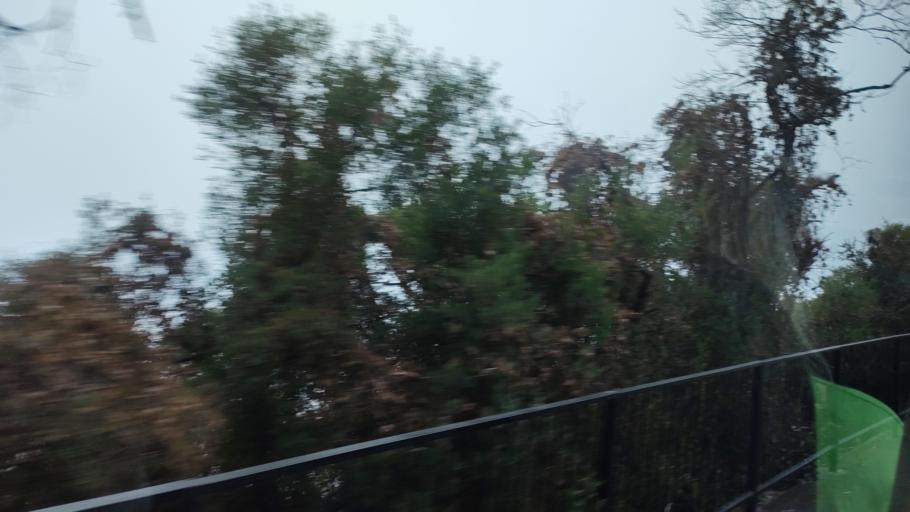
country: GI
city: Gibraltar
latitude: 36.1385
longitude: -5.3484
